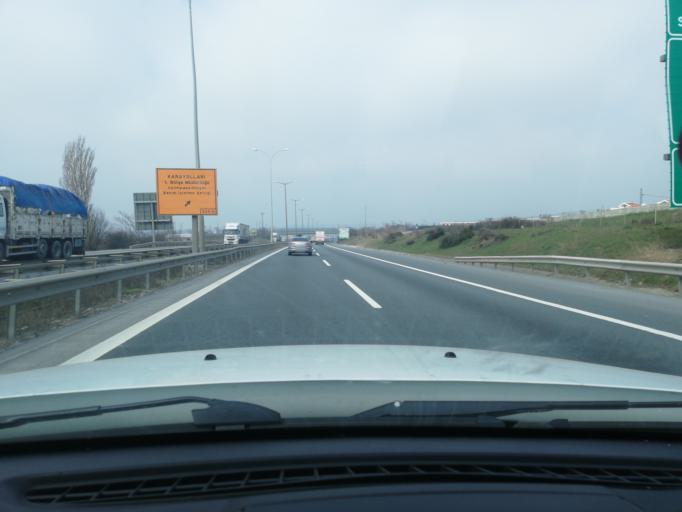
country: TR
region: Istanbul
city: Selimpasa
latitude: 41.0765
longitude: 28.3753
